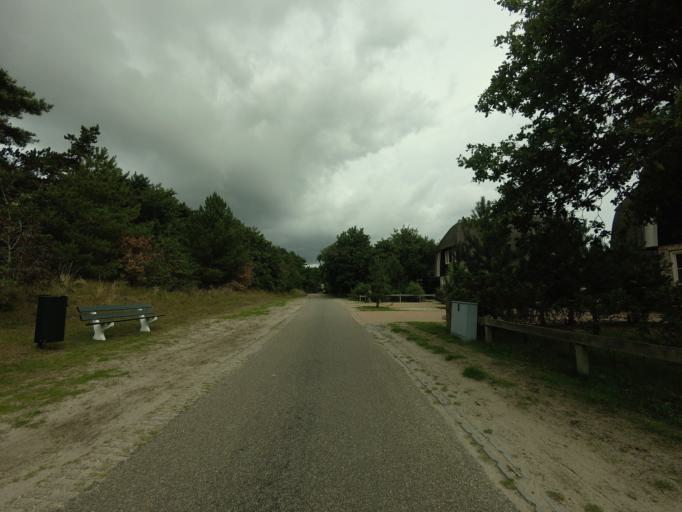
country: NL
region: Friesland
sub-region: Gemeente Ameland
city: Hollum
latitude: 53.4464
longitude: 5.6267
